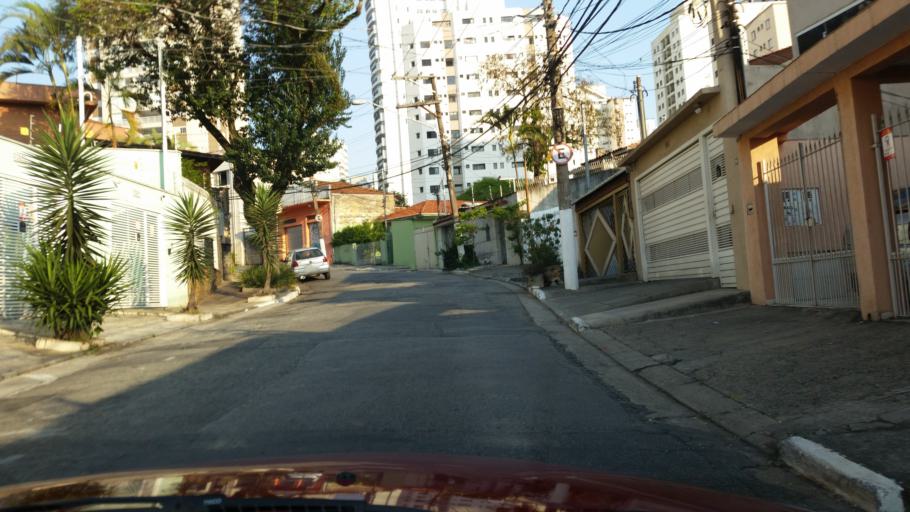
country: BR
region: Sao Paulo
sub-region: Sao Paulo
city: Sao Paulo
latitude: -23.6043
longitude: -46.6233
